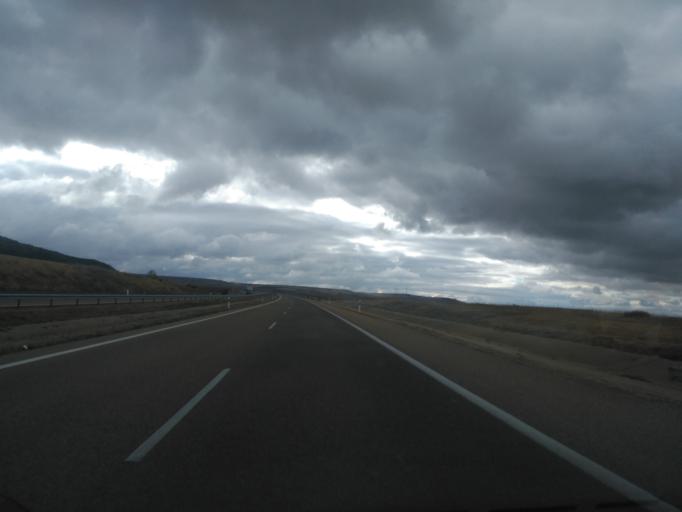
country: ES
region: Castille and Leon
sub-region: Provincia de Palencia
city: Amusco
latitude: 42.1522
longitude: -4.4687
